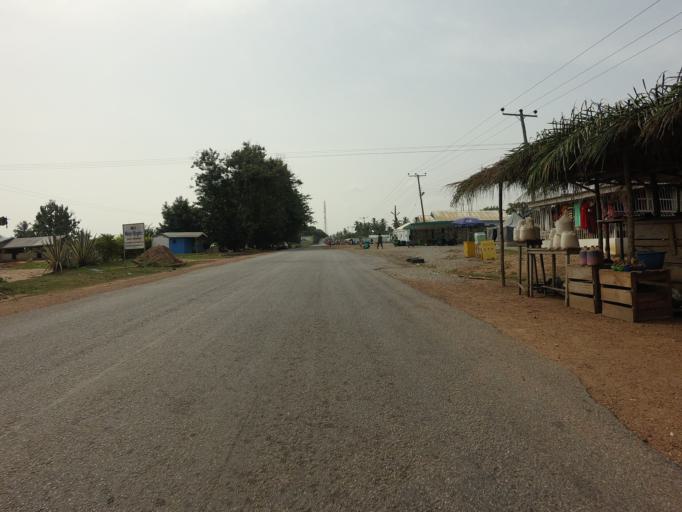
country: GH
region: Volta
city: Ho
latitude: 6.4123
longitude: 0.1724
